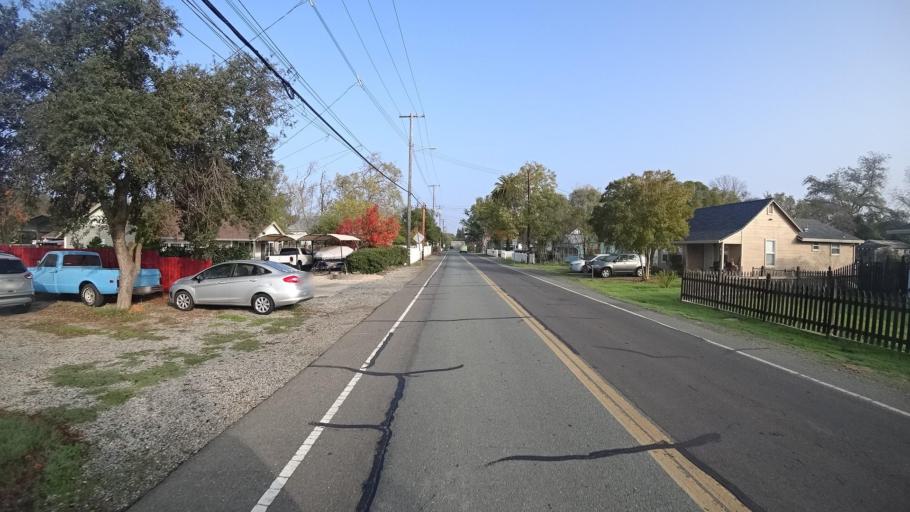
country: US
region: California
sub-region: Sacramento County
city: Elk Grove
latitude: 38.4067
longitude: -121.3595
